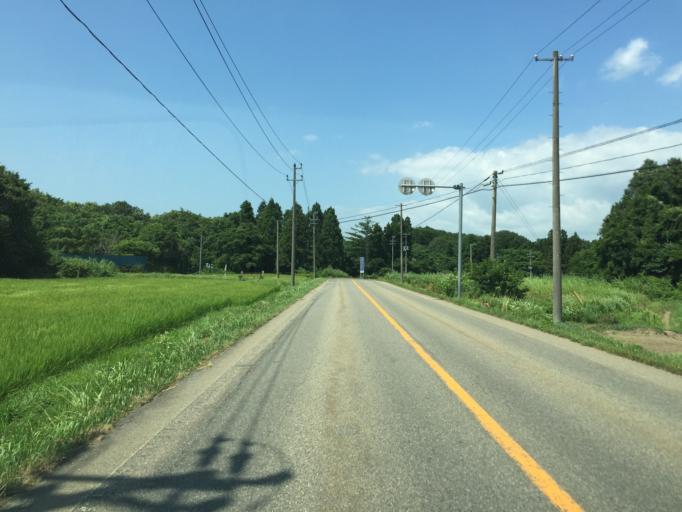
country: JP
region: Fukushima
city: Inawashiro
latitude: 37.5129
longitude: 139.9890
